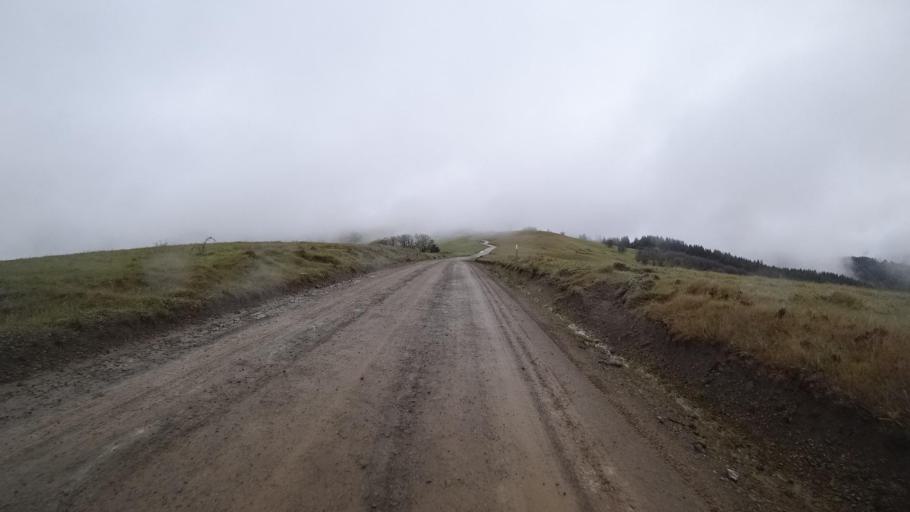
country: US
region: California
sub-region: Humboldt County
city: Westhaven-Moonstone
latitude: 41.1422
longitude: -123.8642
